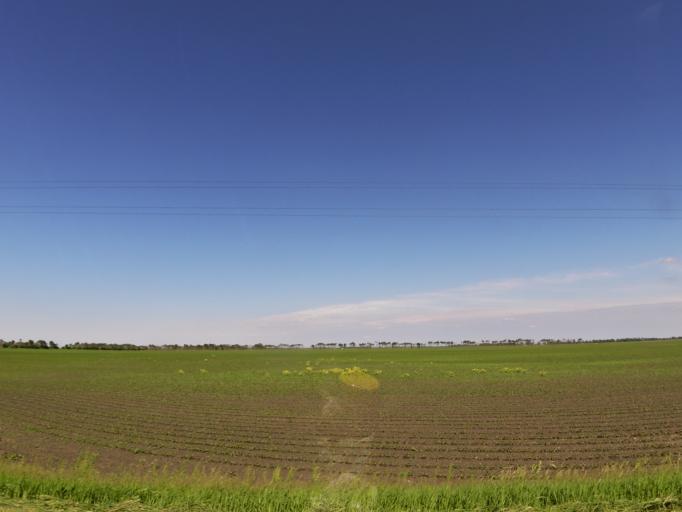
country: US
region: North Dakota
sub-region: Walsh County
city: Grafton
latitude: 48.3134
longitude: -97.2552
